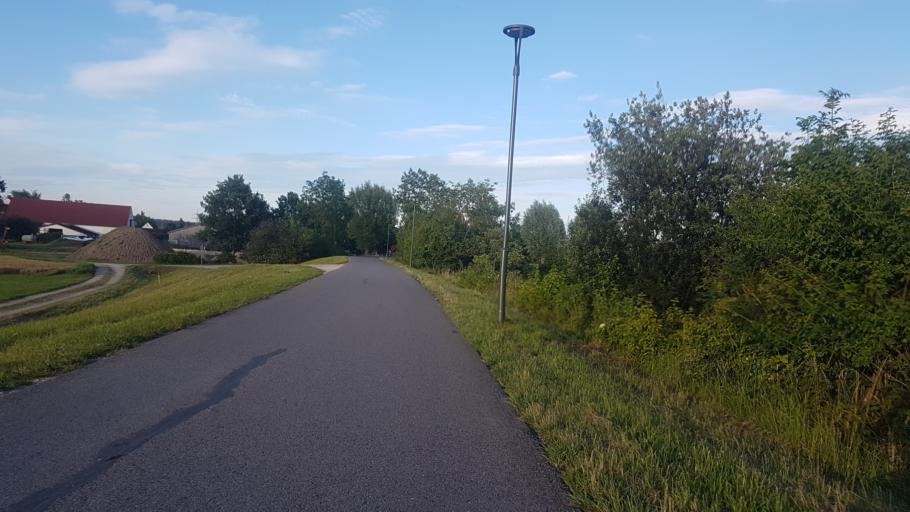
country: DE
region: Bavaria
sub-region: Regierungsbezirk Mittelfranken
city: Gunzenhausen
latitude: 49.1244
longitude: 10.7464
